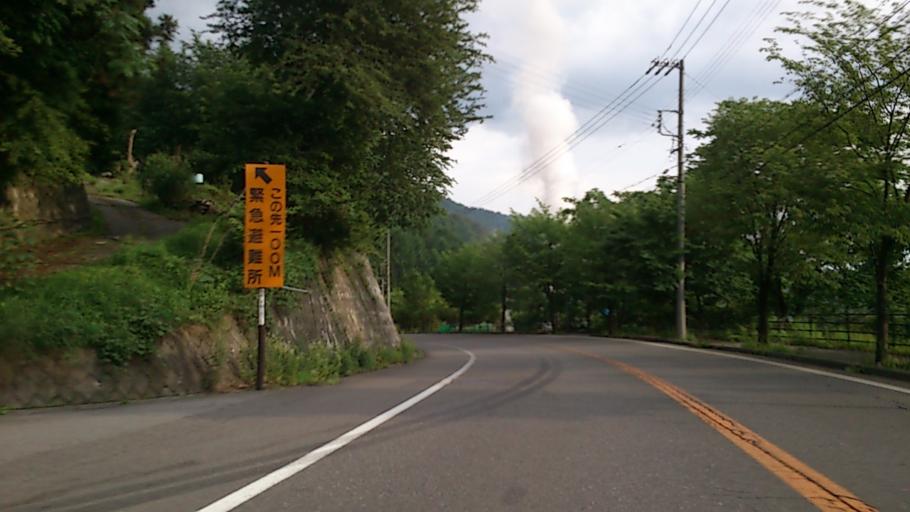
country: JP
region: Nagano
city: Suwa
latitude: 36.1122
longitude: 138.0992
